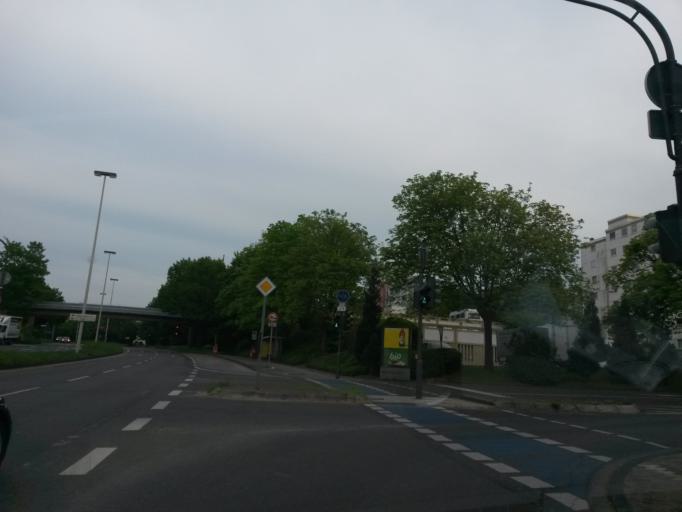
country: DE
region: North Rhine-Westphalia
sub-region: Regierungsbezirk Koln
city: Alfter
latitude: 50.7125
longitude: 7.0302
